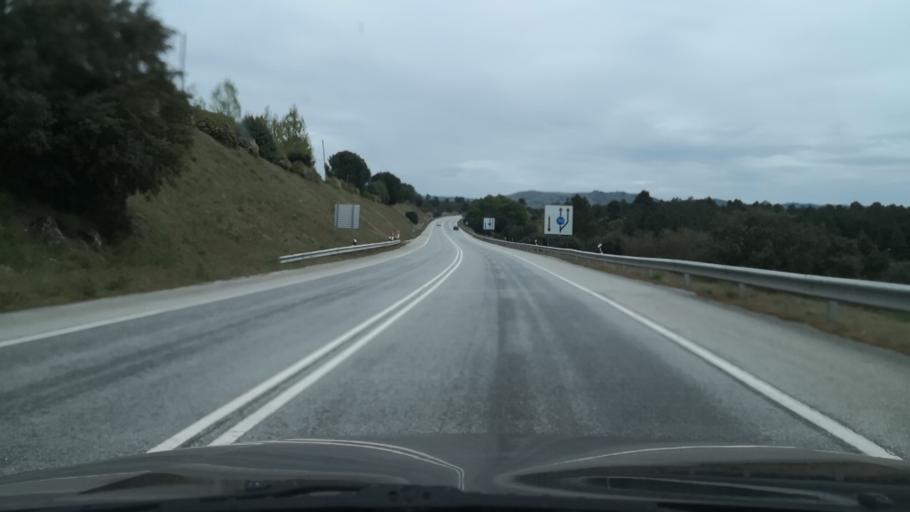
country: PT
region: Guarda
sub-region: Celorico da Beira
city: Celorico da Beira
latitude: 40.6363
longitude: -7.3213
